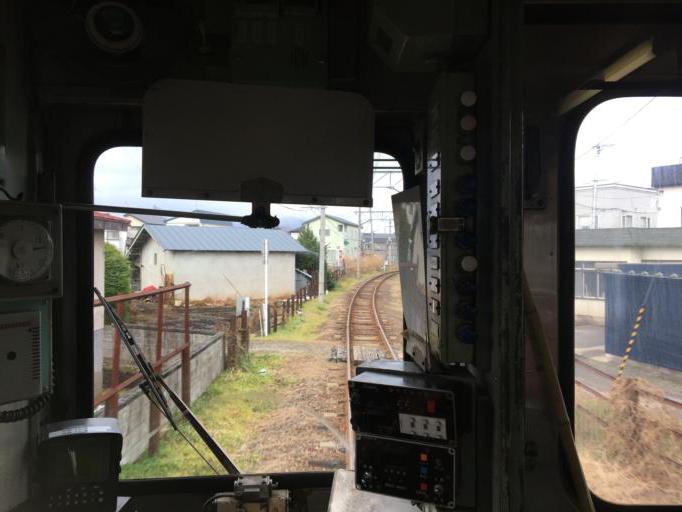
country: JP
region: Aomori
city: Hirosaki
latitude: 40.5680
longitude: 140.4793
